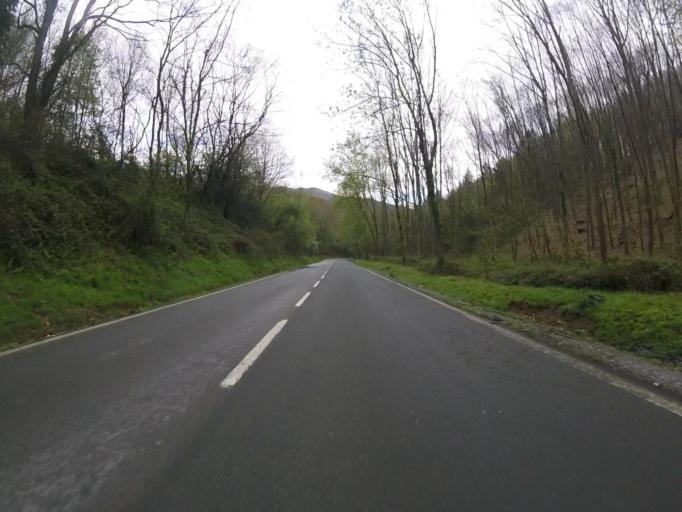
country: ES
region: Navarre
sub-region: Provincia de Navarra
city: Etxalar
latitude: 43.2819
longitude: -1.6300
